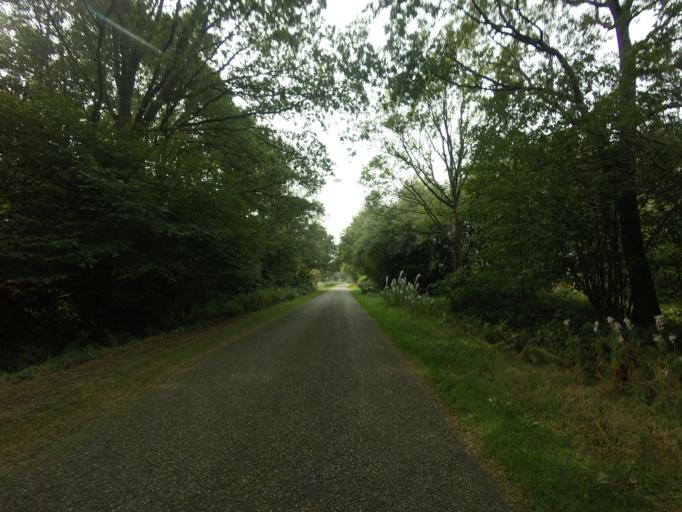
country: NL
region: Drenthe
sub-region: Gemeente Tynaarlo
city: Vries
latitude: 53.1152
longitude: 6.5400
